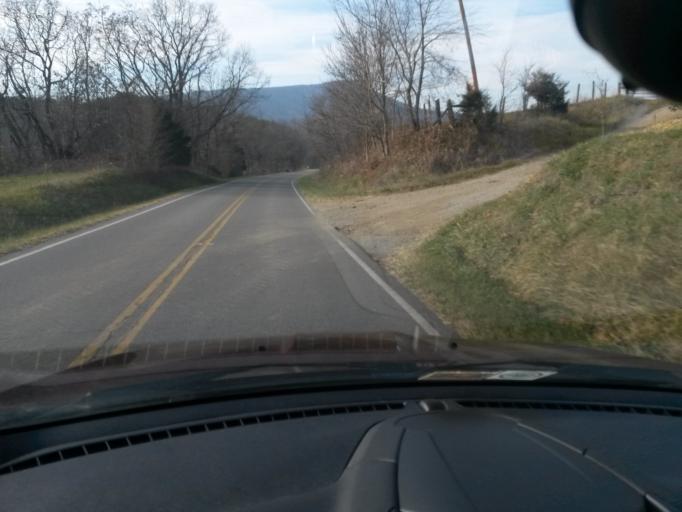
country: US
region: Virginia
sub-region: Botetourt County
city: Daleville
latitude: 37.4540
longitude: -79.9544
